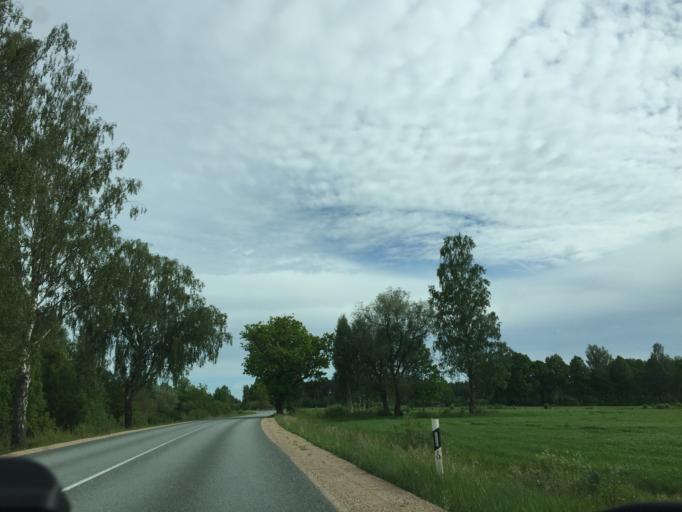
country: LV
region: Beverina
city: Murmuiza
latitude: 57.4574
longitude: 25.4201
